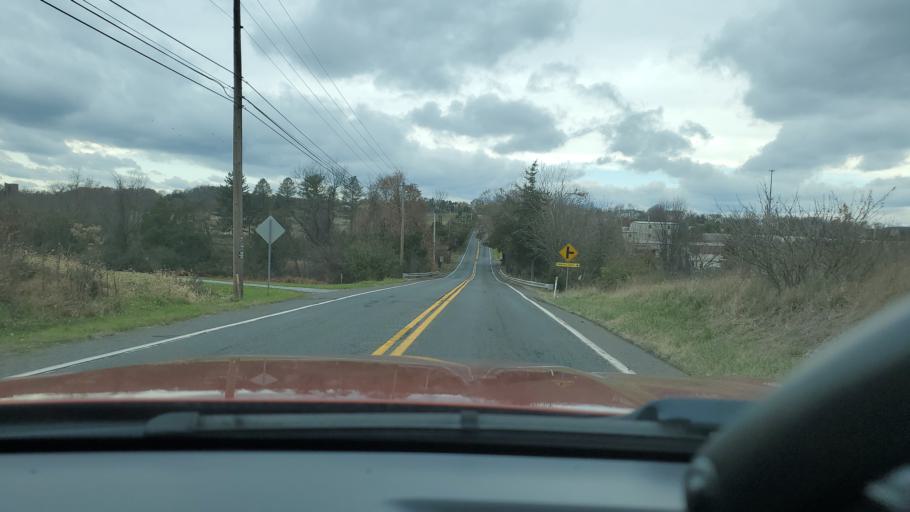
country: US
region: Pennsylvania
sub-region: Montgomery County
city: Spring Mount
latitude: 40.2806
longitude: -75.4992
